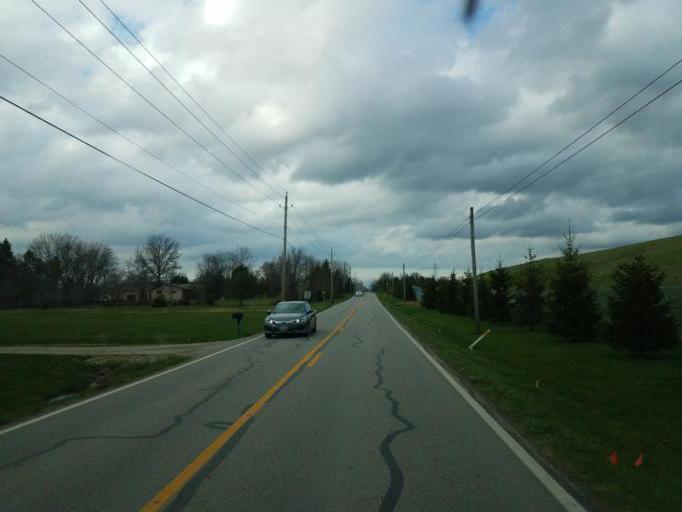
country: US
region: Ohio
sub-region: Delaware County
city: Powell
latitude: 40.2048
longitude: -83.0856
